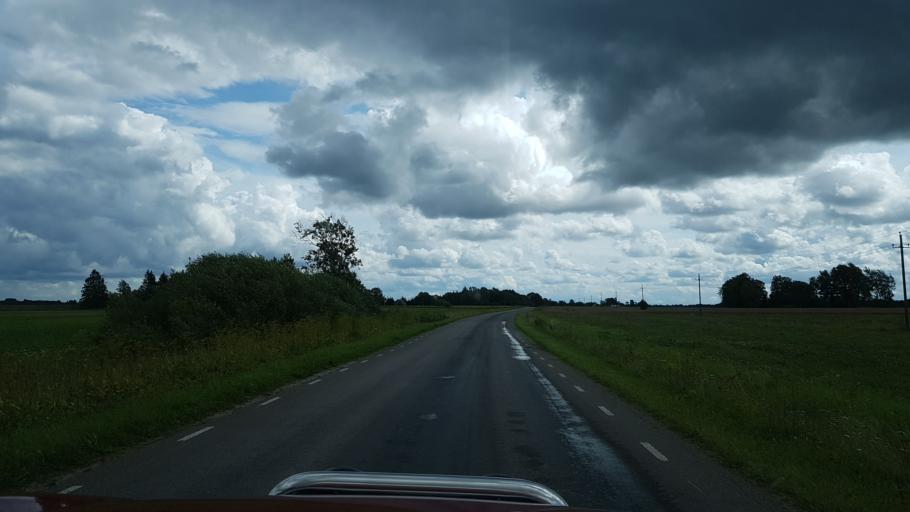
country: EE
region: Laeaene
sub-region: Lihula vald
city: Lihula
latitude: 58.7161
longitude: 23.9939
